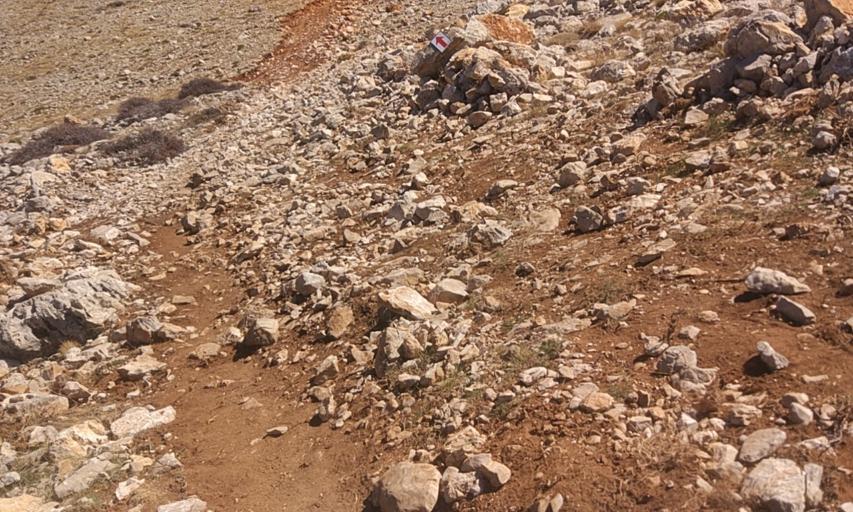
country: TR
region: Antalya
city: Altinyaka
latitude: 36.5410
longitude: 30.4203
